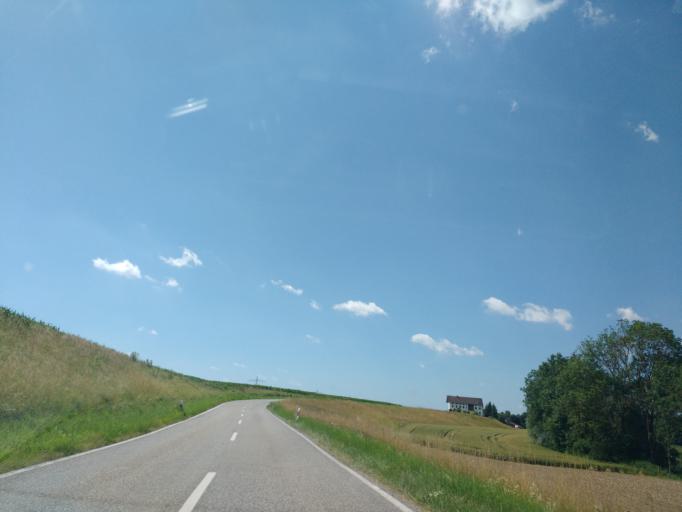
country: DE
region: Bavaria
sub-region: Upper Bavaria
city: Taufkirchen
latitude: 48.1248
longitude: 12.4234
